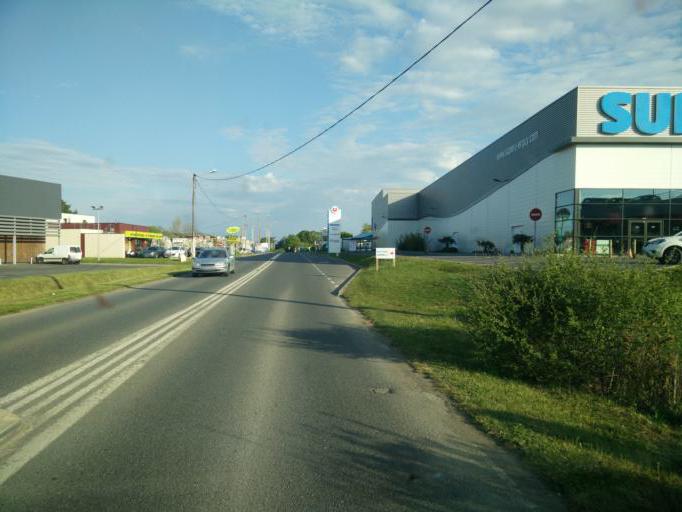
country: FR
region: Brittany
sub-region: Departement des Cotes-d'Armor
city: Erquy
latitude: 48.6222
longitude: -2.4390
